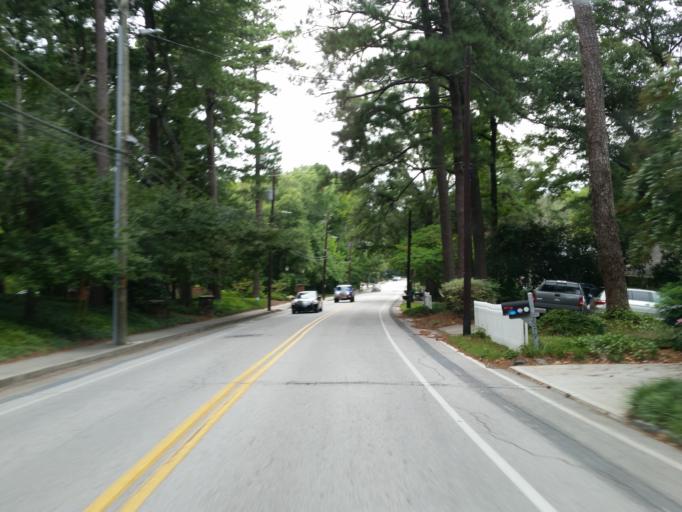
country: US
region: Georgia
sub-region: Fulton County
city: Atlanta
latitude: 33.8118
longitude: -84.4137
